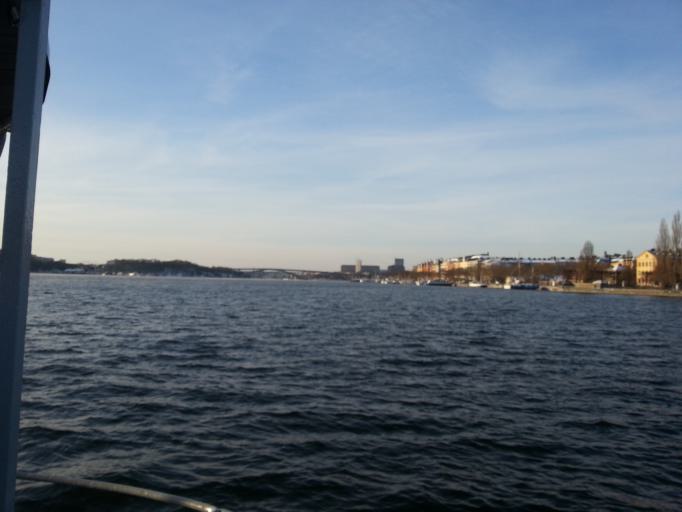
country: SE
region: Stockholm
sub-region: Stockholms Kommun
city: Stockholm
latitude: 59.3258
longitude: 18.0580
